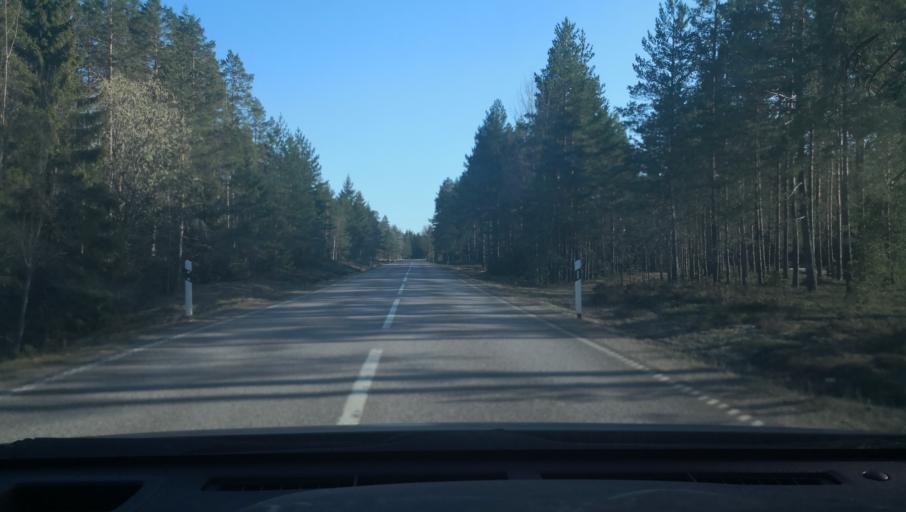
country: SE
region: Uppsala
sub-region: Heby Kommun
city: Tarnsjo
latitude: 60.0831
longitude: 16.8801
